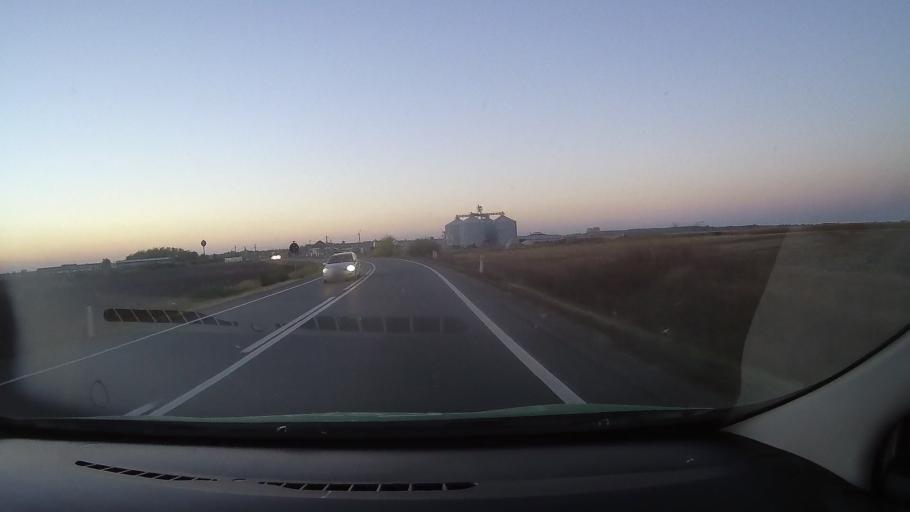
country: RO
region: Bihor
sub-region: Comuna Tarcea
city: Tarcea
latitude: 47.4512
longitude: 22.1839
